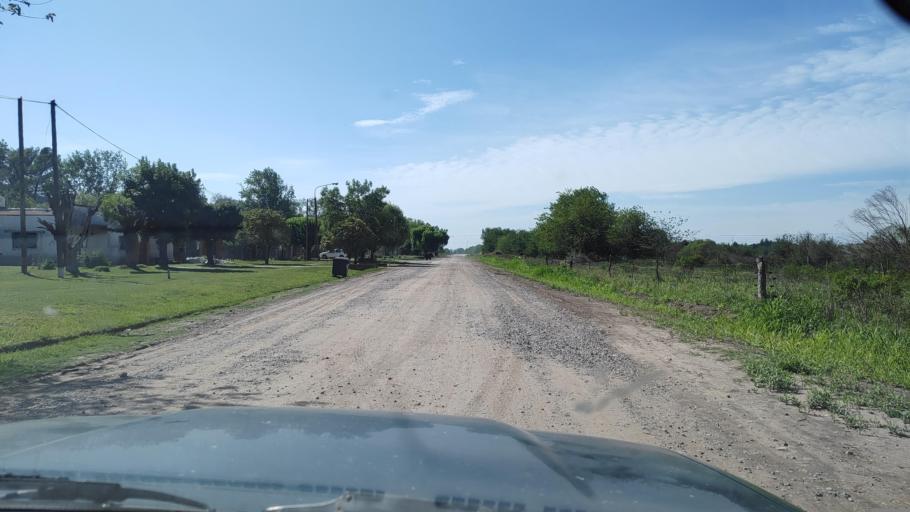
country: AR
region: Buenos Aires
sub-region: Partido de Lujan
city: Lujan
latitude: -34.5465
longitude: -59.1443
